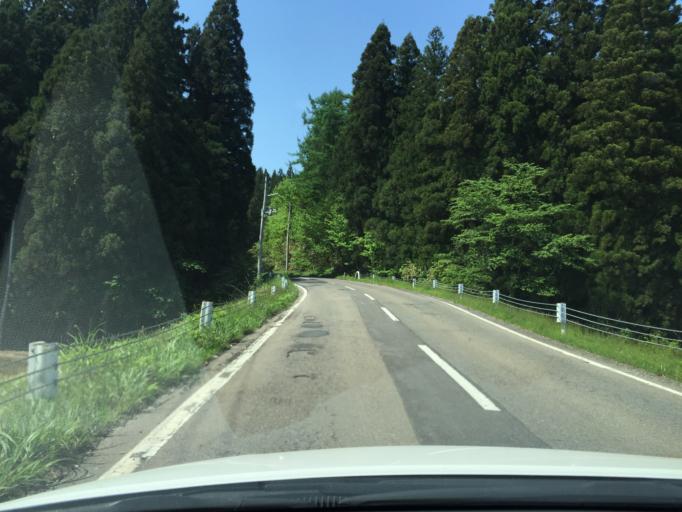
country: JP
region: Niigata
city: Kamo
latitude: 37.5619
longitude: 139.0834
